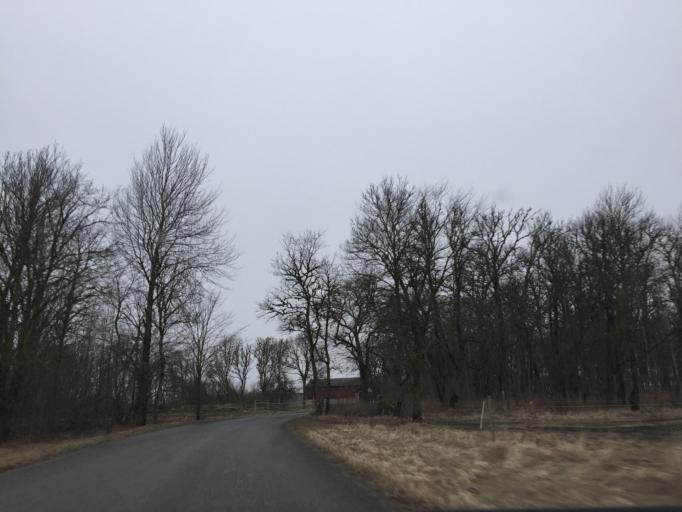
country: EE
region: Laeaene
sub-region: Lihula vald
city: Lihula
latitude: 58.6492
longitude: 23.6171
